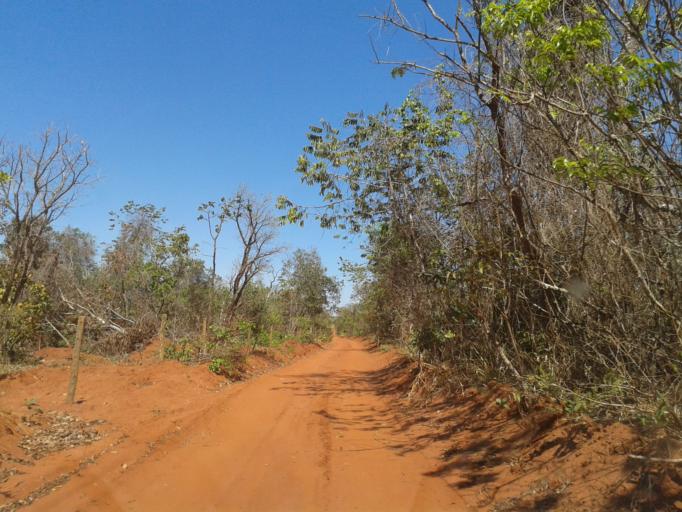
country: BR
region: Minas Gerais
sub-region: Ituiutaba
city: Ituiutaba
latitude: -19.0967
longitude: -49.2688
